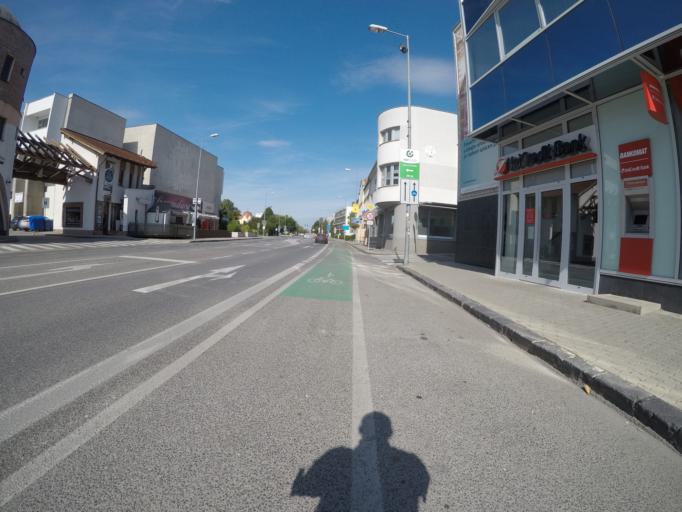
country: SK
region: Trnavsky
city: Dunajska Streda
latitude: 47.9947
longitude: 17.6171
